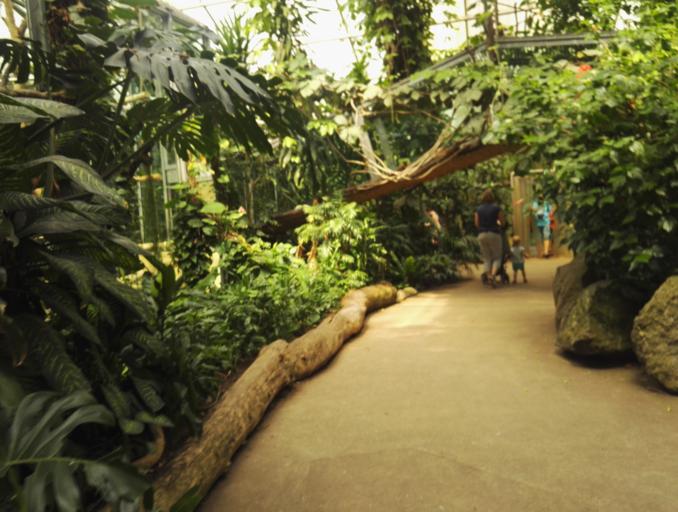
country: DE
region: North Rhine-Westphalia
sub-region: Regierungsbezirk Koln
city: Riehl
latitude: 50.9635
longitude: 6.9801
